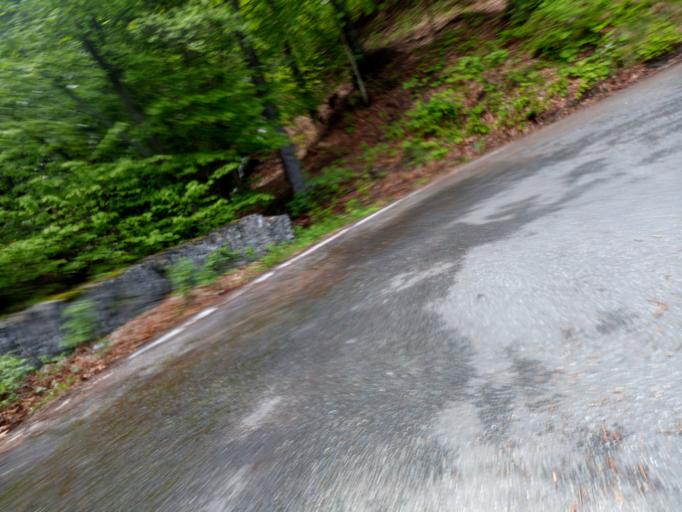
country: IT
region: Piedmont
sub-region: Provincia di Torino
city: Meana di Susa
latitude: 45.1101
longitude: 7.0622
